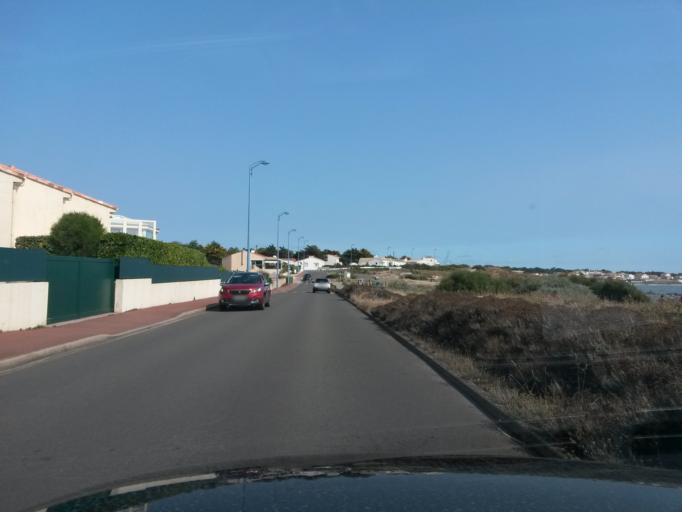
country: FR
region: Pays de la Loire
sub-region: Departement de la Vendee
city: Bretignolles-sur-Mer
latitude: 46.6318
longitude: -1.8836
